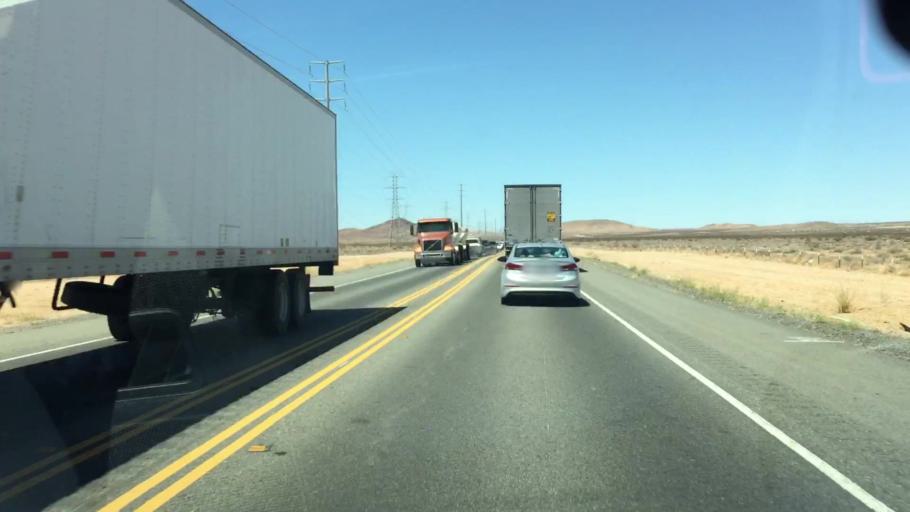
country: US
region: California
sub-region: Kern County
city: Boron
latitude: 34.8367
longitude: -117.4984
